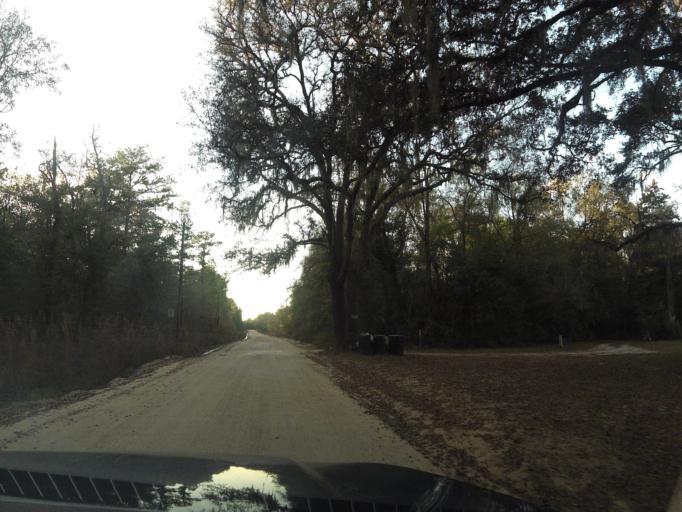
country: US
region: Florida
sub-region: Putnam County
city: Interlachen
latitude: 29.7811
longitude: -81.8592
